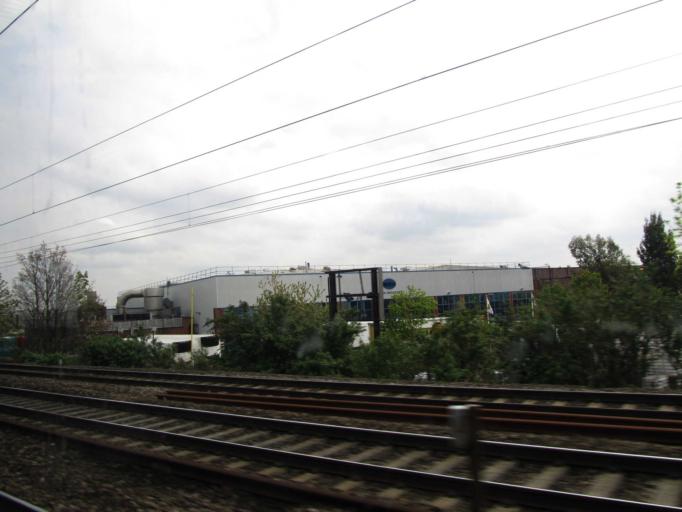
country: GB
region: England
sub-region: Greater London
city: Southall
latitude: 51.5078
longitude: -0.3648
